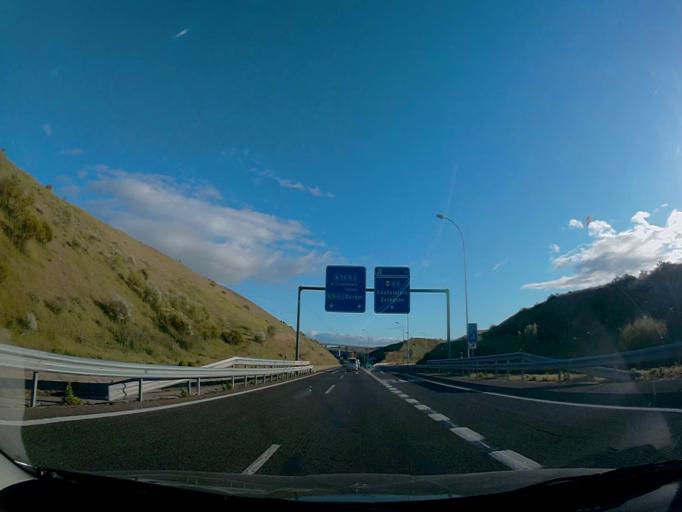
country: ES
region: Madrid
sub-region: Provincia de Madrid
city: Ajalvir
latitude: 40.5049
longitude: -3.4941
